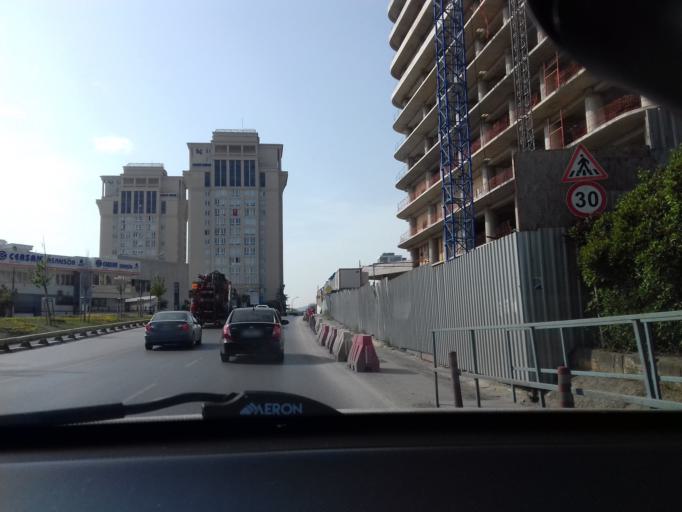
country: TR
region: Istanbul
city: Maltepe
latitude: 40.9089
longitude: 29.2131
